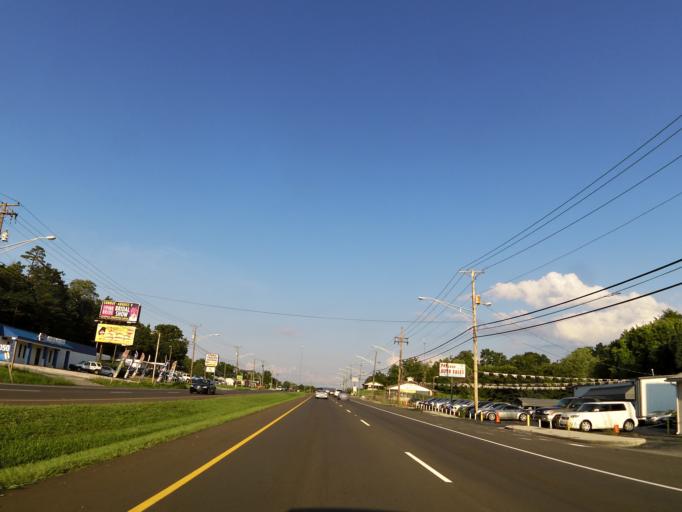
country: US
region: Tennessee
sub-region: Knox County
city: Knoxville
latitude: 36.0087
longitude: -83.9989
